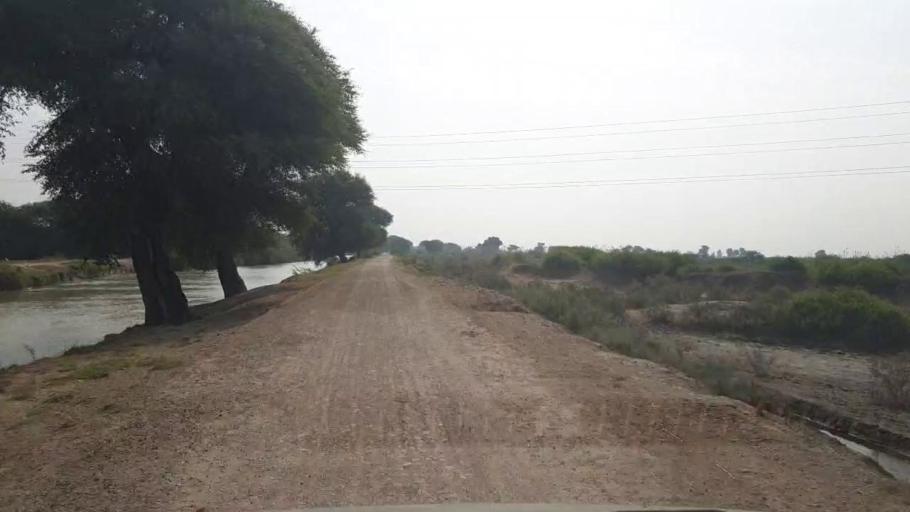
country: PK
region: Sindh
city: Tando Muhammad Khan
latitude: 25.1262
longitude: 68.4361
